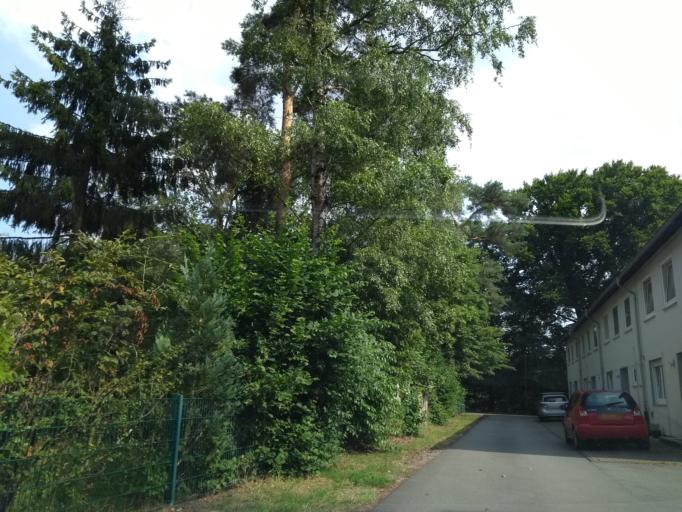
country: DE
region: North Rhine-Westphalia
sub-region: Regierungsbezirk Detmold
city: Paderborn
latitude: 51.7732
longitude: 8.7304
